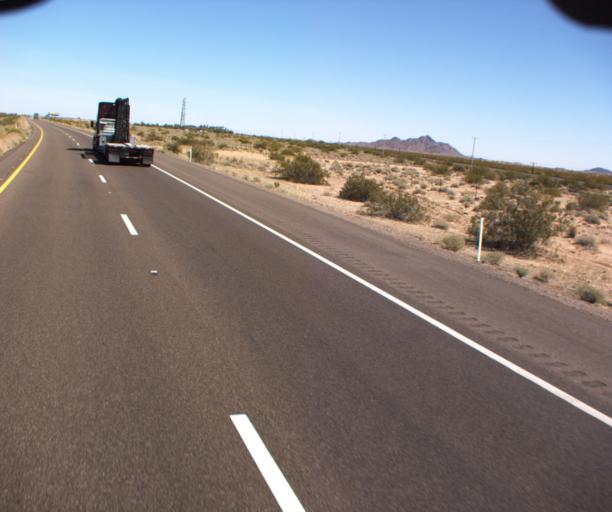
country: US
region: Arizona
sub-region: Yuma County
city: Wellton
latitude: 32.7906
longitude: -113.5574
